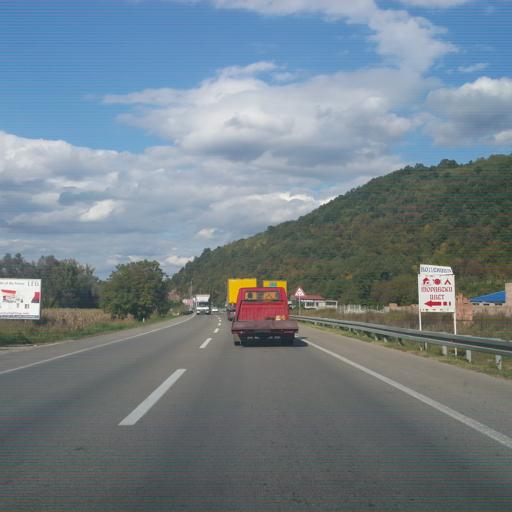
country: RS
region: Central Serbia
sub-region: Rasinski Okrug
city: Krusevac
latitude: 43.6245
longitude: 21.3741
